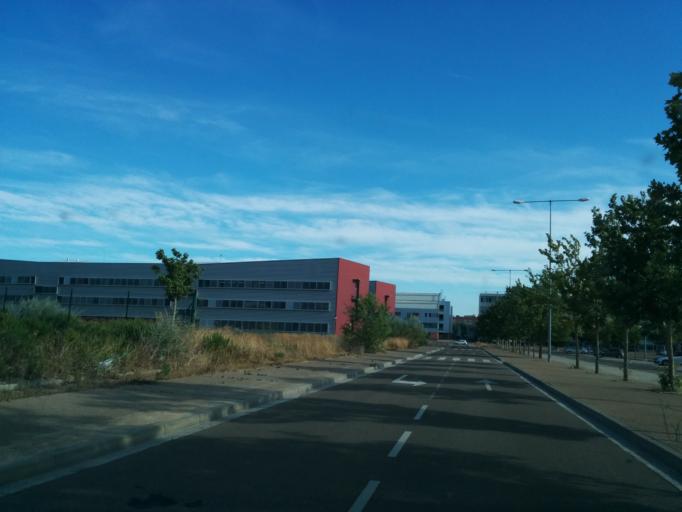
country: ES
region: Aragon
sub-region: Provincia de Zaragoza
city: Almozara
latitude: 41.6862
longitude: -0.8883
